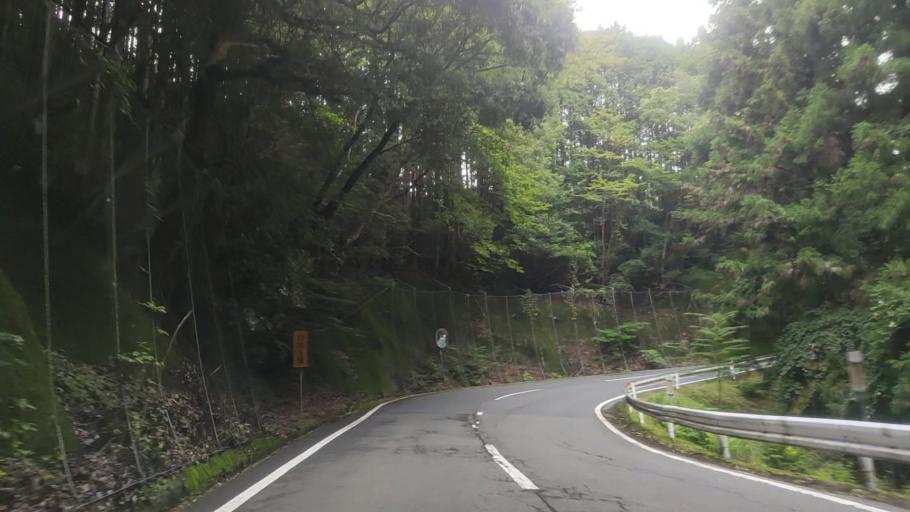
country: JP
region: Wakayama
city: Koya
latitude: 34.2136
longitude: 135.5416
